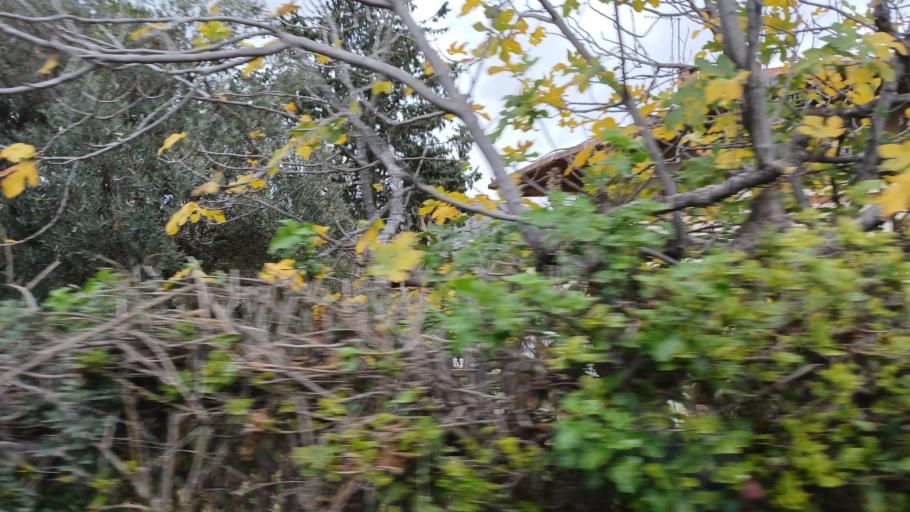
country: CY
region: Limassol
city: Pyrgos
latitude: 34.7767
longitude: 33.2540
